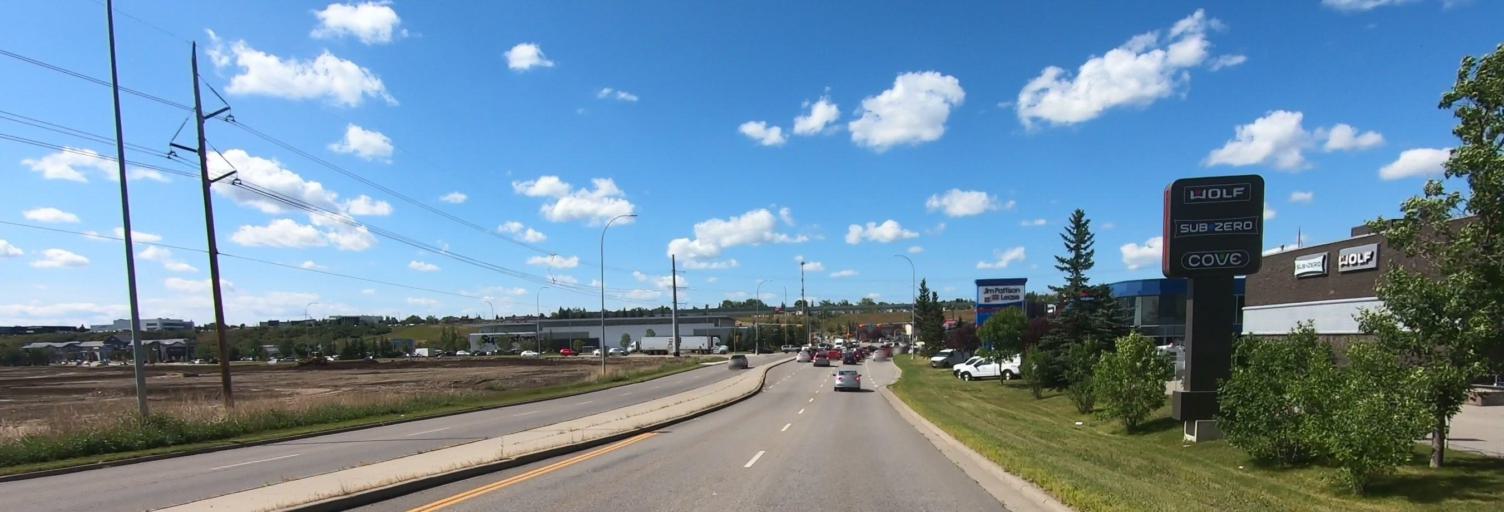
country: CA
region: Alberta
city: Calgary
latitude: 50.9872
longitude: -114.0374
